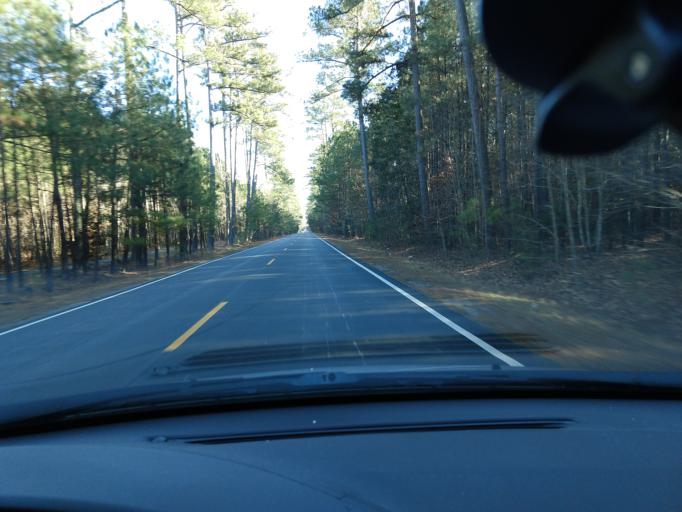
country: US
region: Virginia
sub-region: Surry County
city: Surry
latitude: 37.2807
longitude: -76.9168
